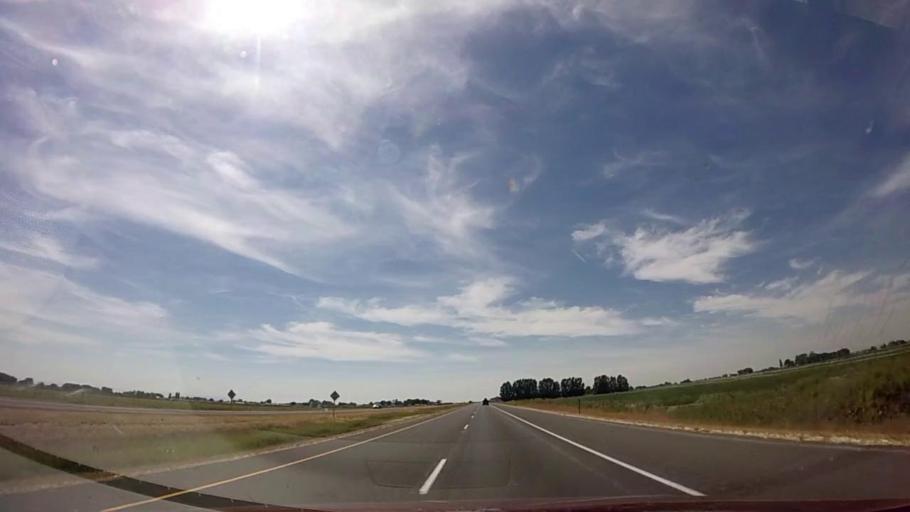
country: US
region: Idaho
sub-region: Minidoka County
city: Rupert
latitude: 42.5690
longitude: -113.6780
